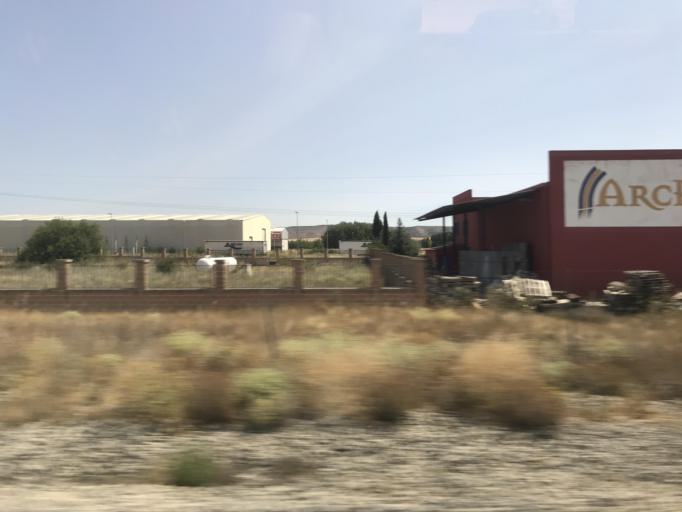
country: ES
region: Castille and Leon
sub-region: Provincia de Palencia
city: Duenas
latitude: 41.8491
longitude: -4.5546
